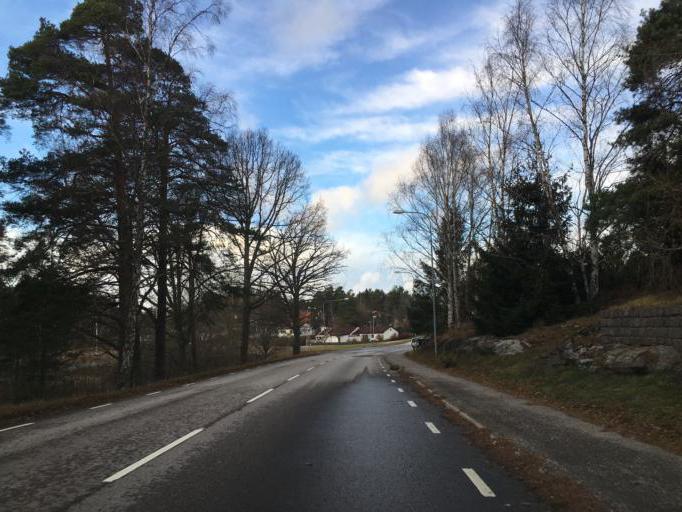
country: SE
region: Kalmar
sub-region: Vasterviks Kommun
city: Vaestervik
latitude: 57.7202
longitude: 16.5275
